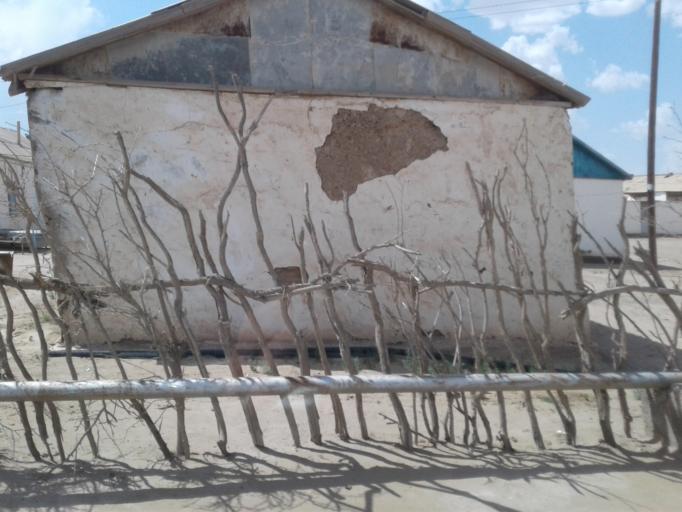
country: TM
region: Ahal
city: Abadan
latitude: 38.7650
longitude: 58.4931
